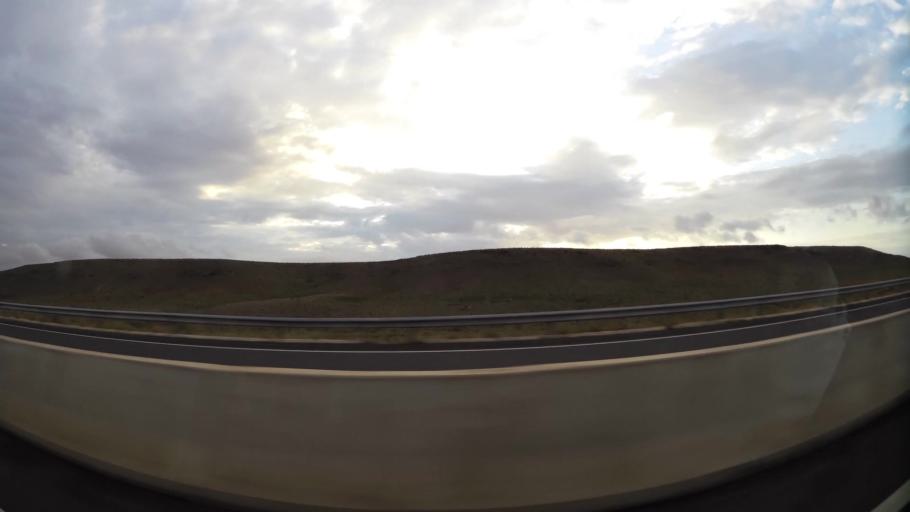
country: MA
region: Oriental
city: Taourirt
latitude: 34.4607
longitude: -3.0444
